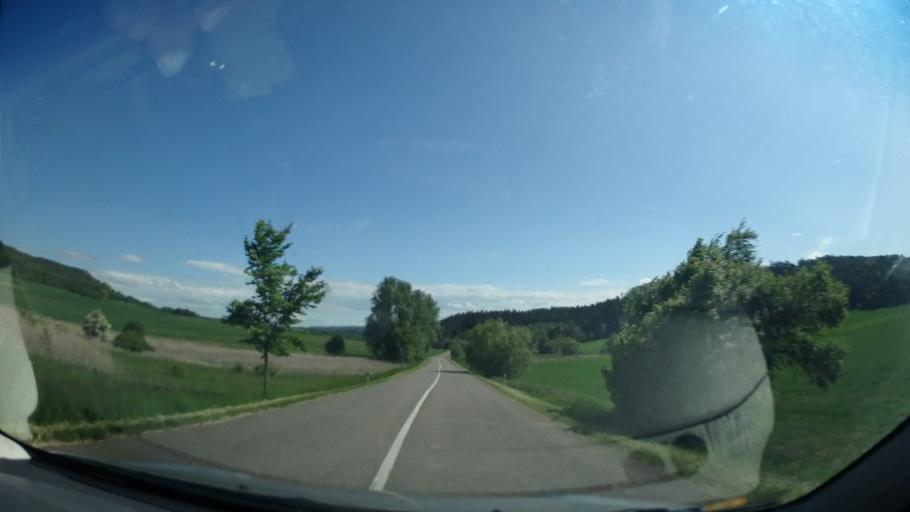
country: CZ
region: South Moravian
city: Velke Opatovice
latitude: 49.6354
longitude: 16.6087
